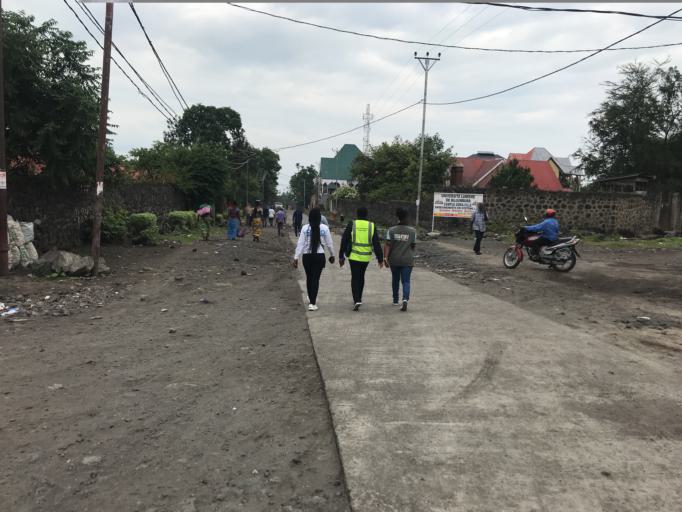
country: CD
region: Nord Kivu
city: Goma
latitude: -1.6862
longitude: 29.2331
